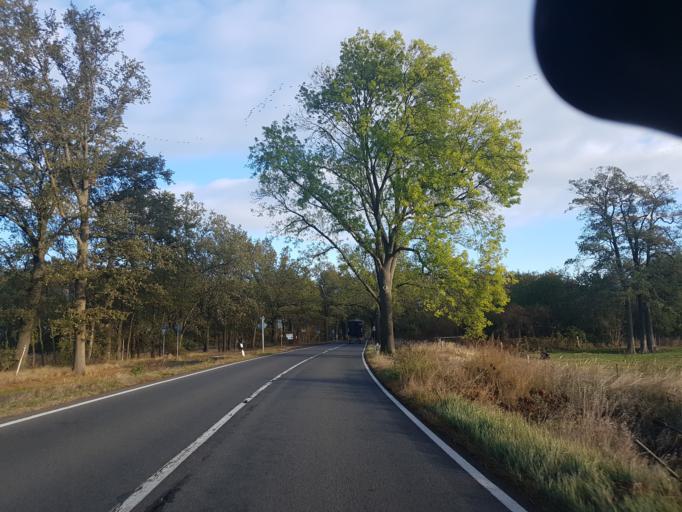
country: DE
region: Brandenburg
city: Nauen
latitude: 52.6582
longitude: 12.9220
